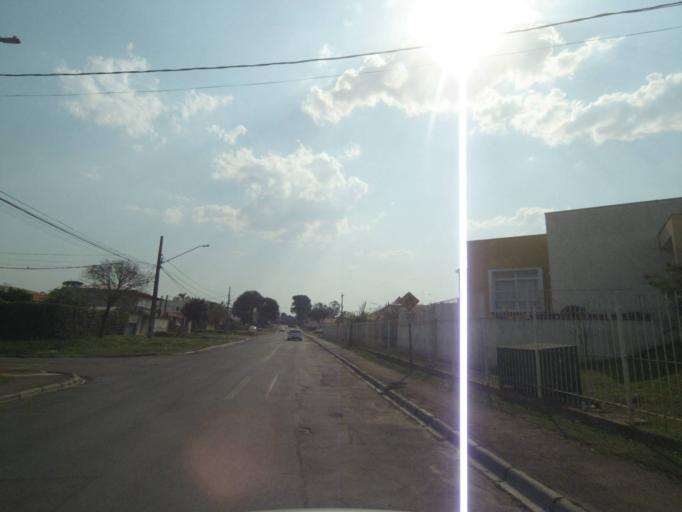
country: BR
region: Parana
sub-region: Sao Jose Dos Pinhais
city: Sao Jose dos Pinhais
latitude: -25.5345
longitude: -49.2396
